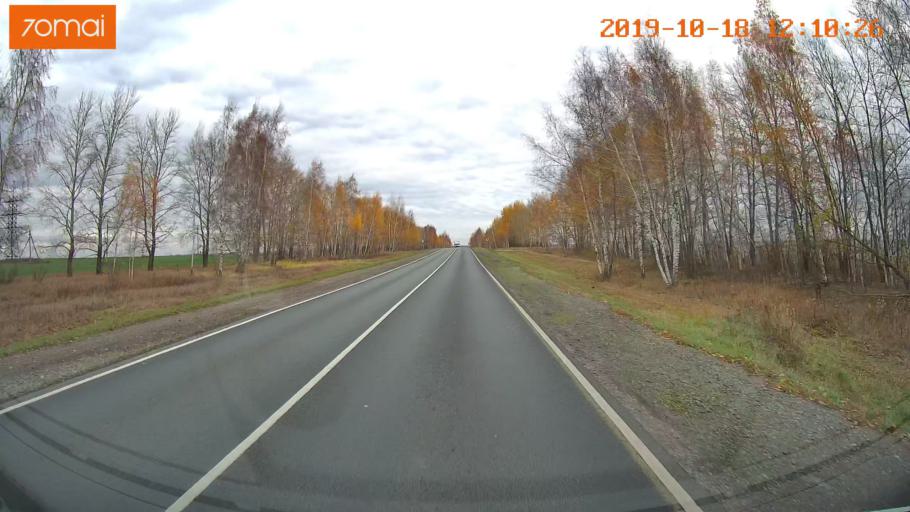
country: RU
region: Rjazan
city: Zakharovo
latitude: 54.3923
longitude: 39.3308
